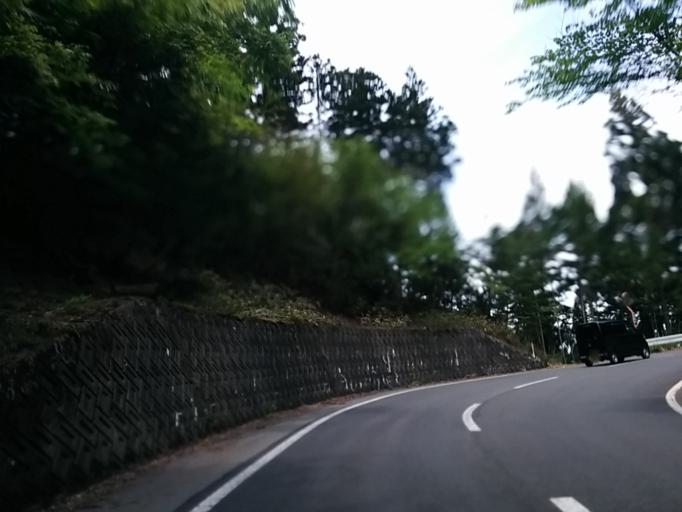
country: JP
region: Gifu
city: Gujo
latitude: 35.7409
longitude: 136.9543
